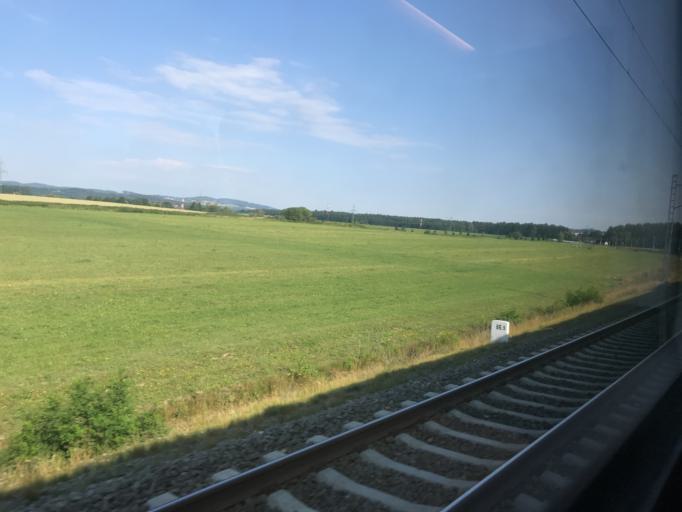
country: CZ
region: Jihocesky
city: Chotoviny
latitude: 49.4451
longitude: 14.6905
